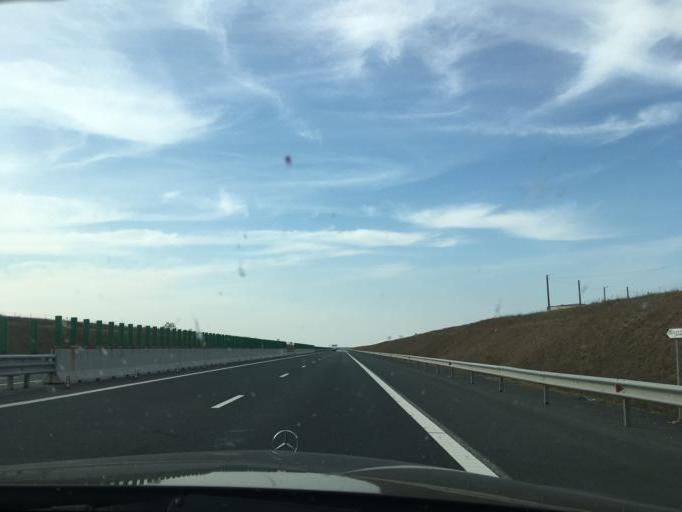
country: RO
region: Constanta
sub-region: Municipiul Medgidia
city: Valea Dacilor
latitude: 44.1855
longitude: 28.3066
